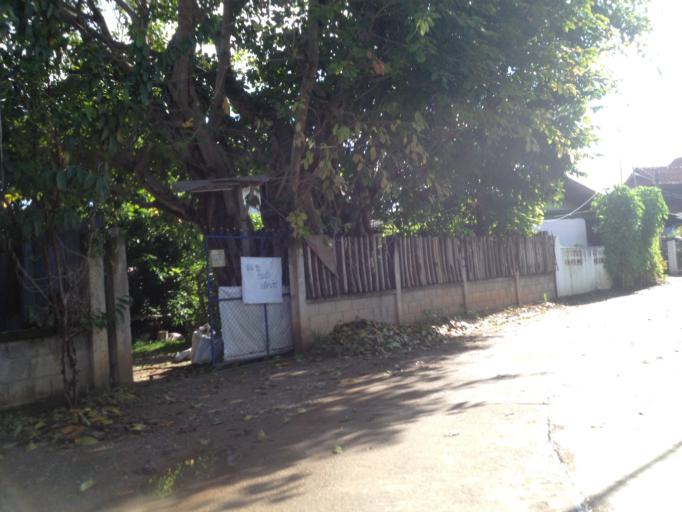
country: TH
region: Chiang Mai
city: Hang Dong
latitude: 18.6974
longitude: 98.9158
